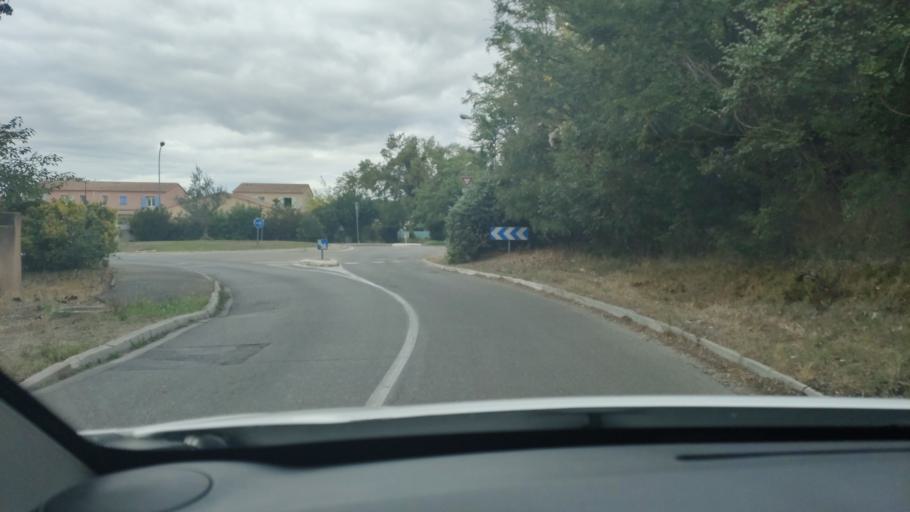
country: FR
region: Provence-Alpes-Cote d'Azur
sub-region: Departement du Vaucluse
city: Le Pontet
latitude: 43.9597
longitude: 4.8832
